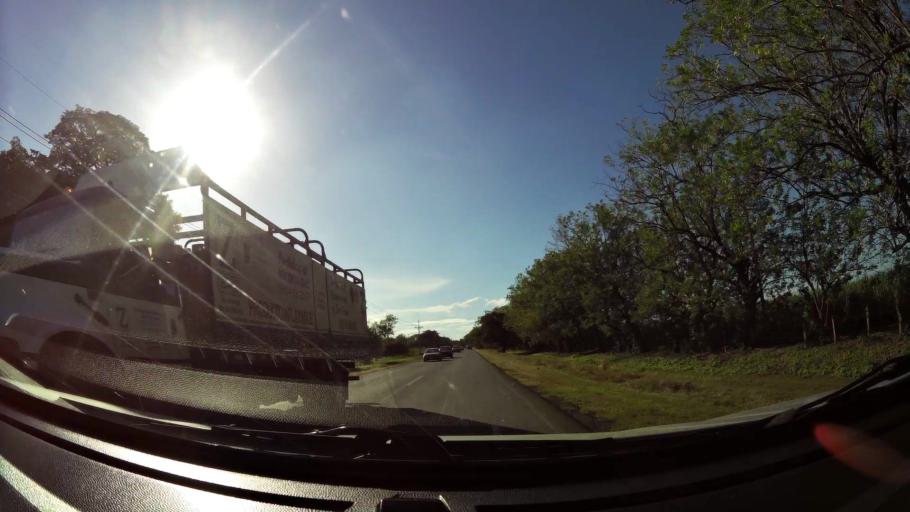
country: CR
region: Guanacaste
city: Belen
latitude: 10.4848
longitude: -85.5670
